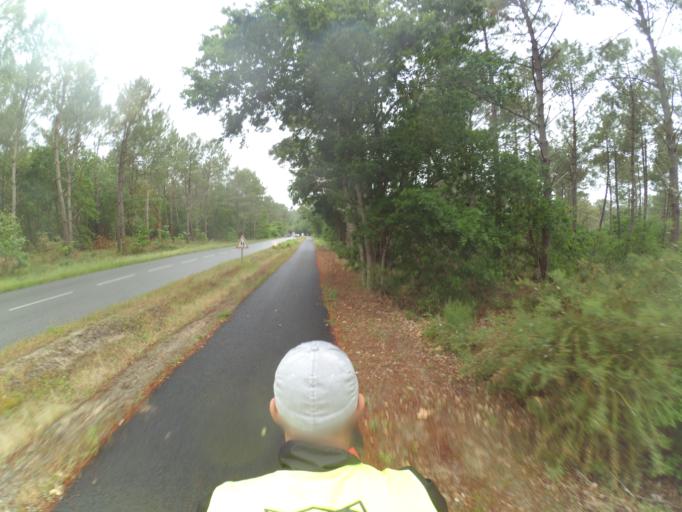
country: FR
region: Aquitaine
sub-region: Departement des Landes
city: Mimizan
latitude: 44.2352
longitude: -1.2207
